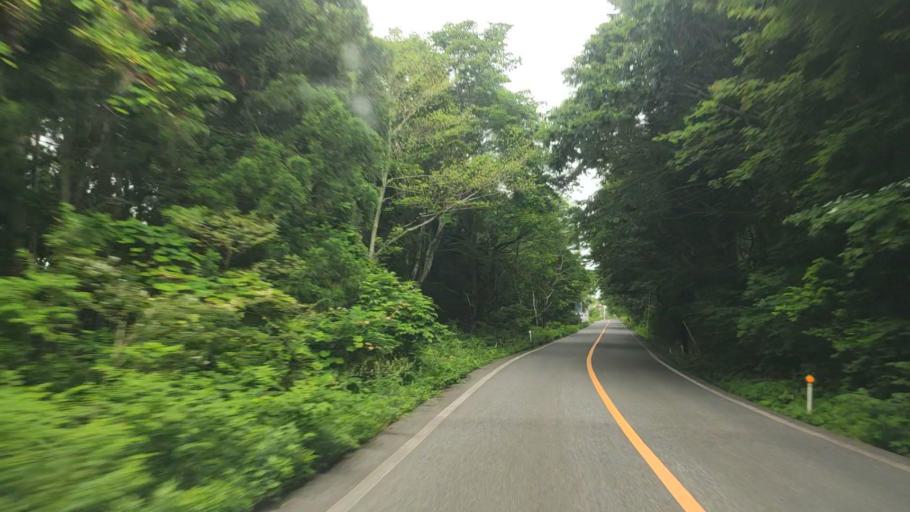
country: JP
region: Tottori
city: Yonago
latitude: 35.3592
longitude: 133.5282
